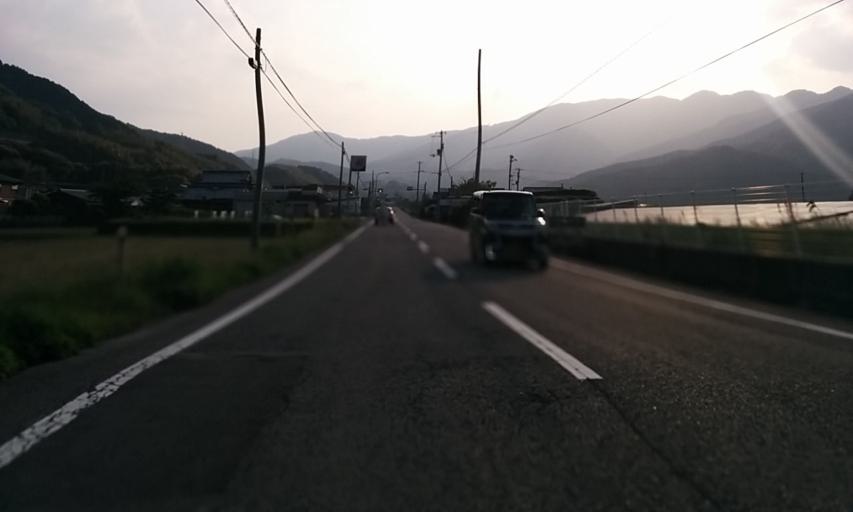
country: JP
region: Ehime
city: Saijo
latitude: 33.8584
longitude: 133.0279
